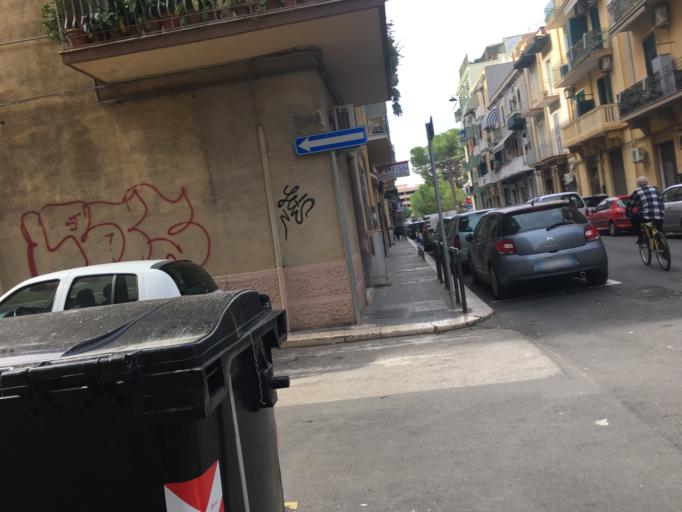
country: IT
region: Apulia
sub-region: Provincia di Bari
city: Bari
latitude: 41.1086
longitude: 16.8687
